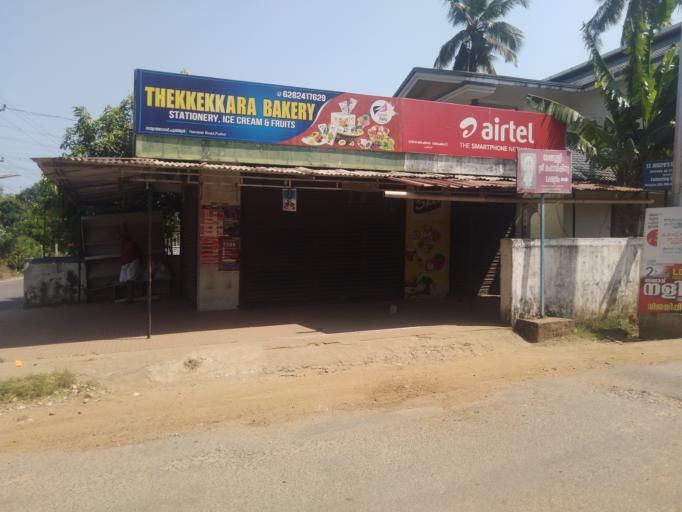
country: IN
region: Kerala
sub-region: Thrissur District
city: Trichur
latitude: 10.4899
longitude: 76.2833
